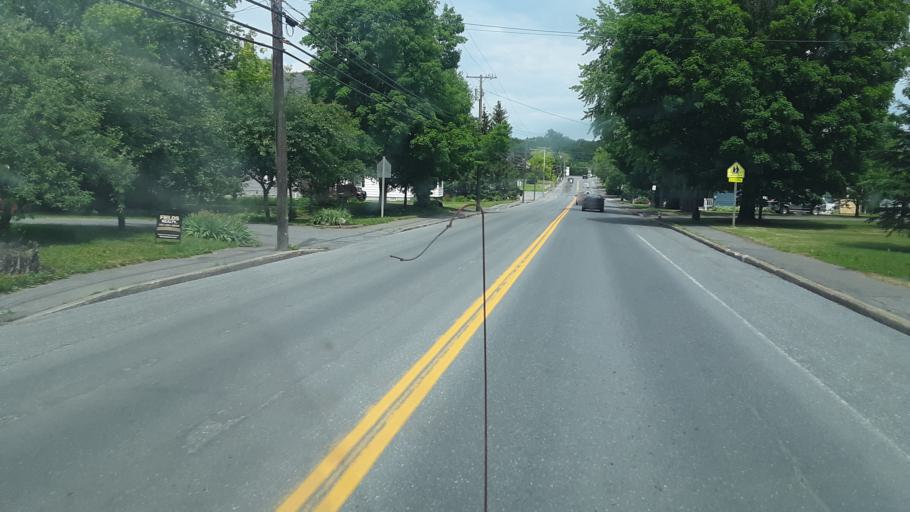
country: US
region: Maine
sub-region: Aroostook County
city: Fort Fairfield
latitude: 46.7706
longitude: -67.8394
